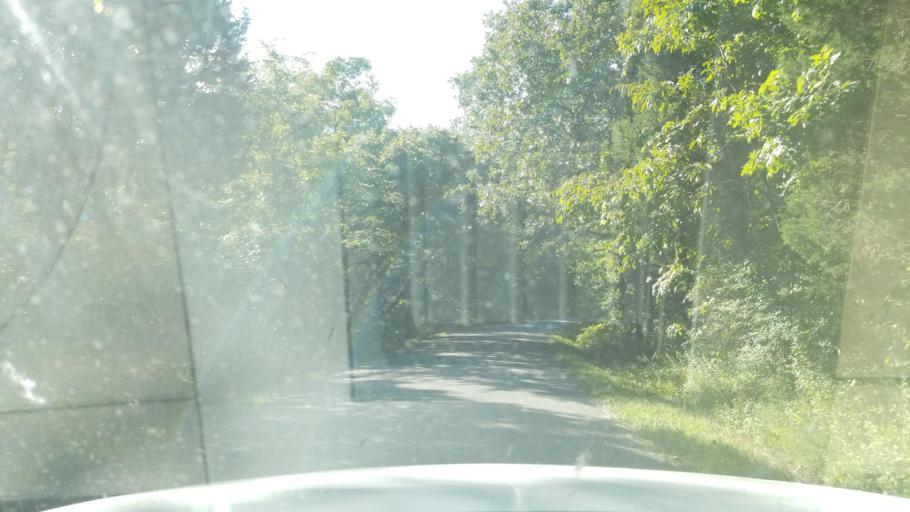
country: US
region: Illinois
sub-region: Hardin County
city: Elizabethtown
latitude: 37.6009
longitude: -88.3812
